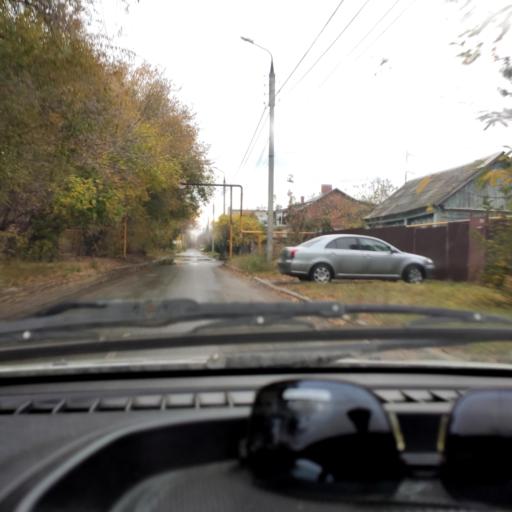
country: RU
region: Samara
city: Tol'yatti
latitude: 53.5303
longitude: 49.4278
